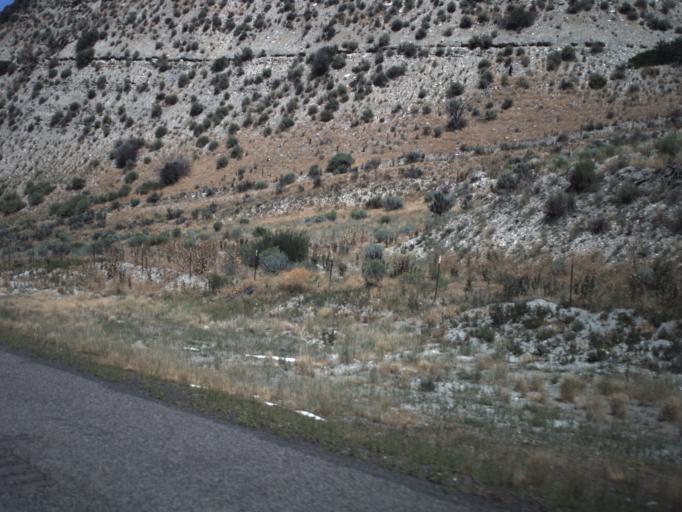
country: US
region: Utah
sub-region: Utah County
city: Mapleton
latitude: 39.9527
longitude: -111.2906
